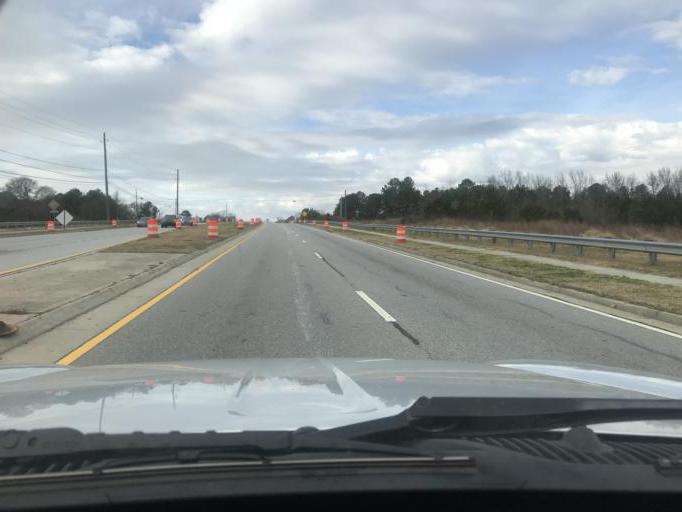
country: US
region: Georgia
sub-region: Gwinnett County
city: Buford
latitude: 34.0616
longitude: -83.9449
